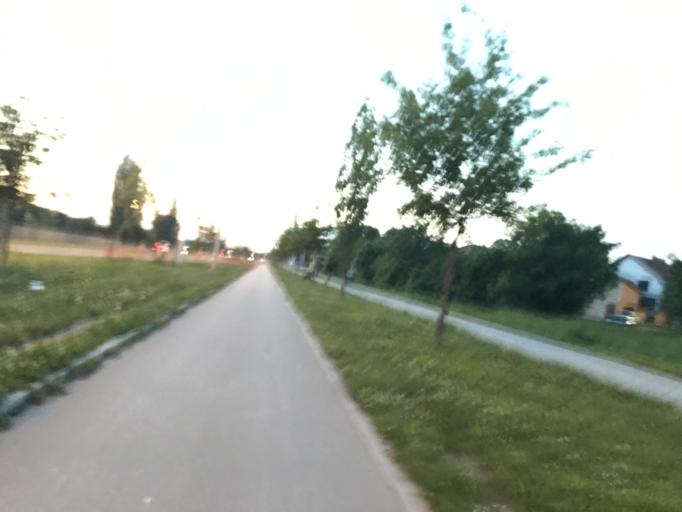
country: RS
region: Autonomna Pokrajina Vojvodina
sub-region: Juznobacki Okrug
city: Novi Sad
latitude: 45.2673
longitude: 19.8041
